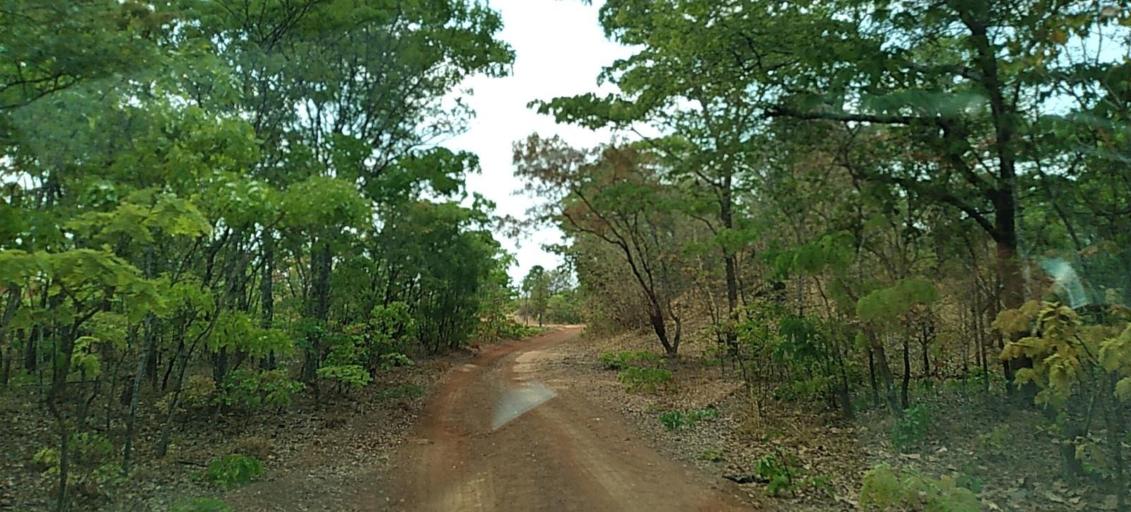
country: ZM
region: Copperbelt
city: Chililabombwe
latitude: -12.4944
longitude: 27.6369
